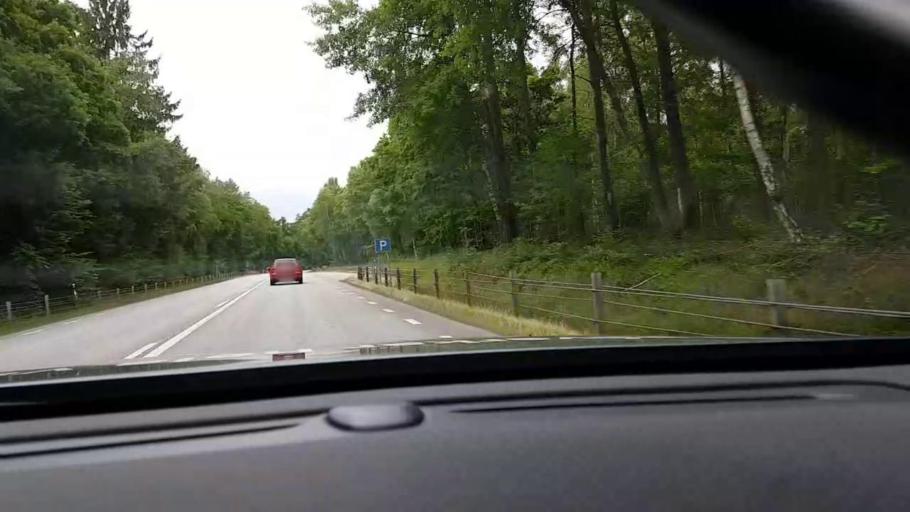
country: SE
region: Skane
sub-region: Hoors Kommun
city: Satofta
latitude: 55.9136
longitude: 13.5976
